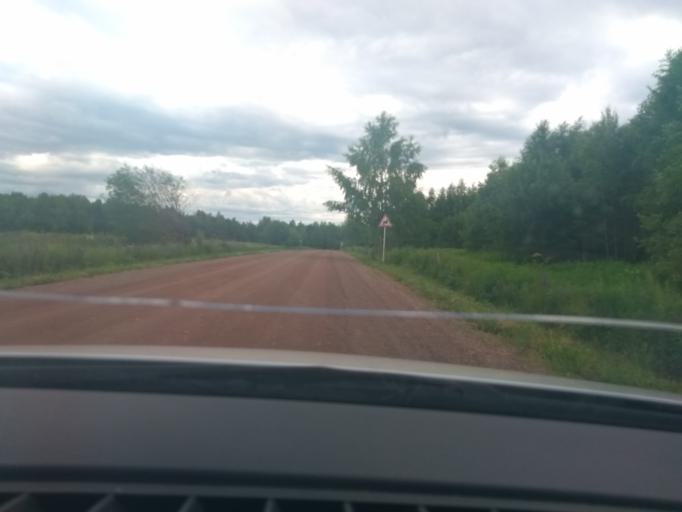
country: RU
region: Perm
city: Sylva
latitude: 57.8163
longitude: 56.7287
